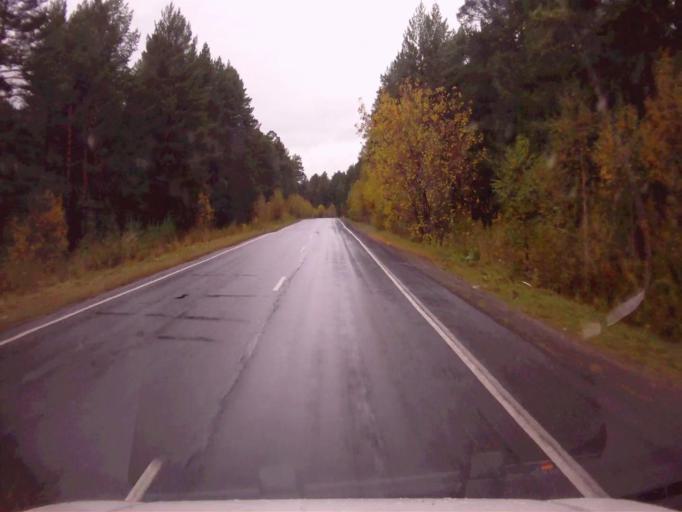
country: RU
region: Chelyabinsk
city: Verkhniy Ufaley
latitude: 56.0508
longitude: 60.1623
